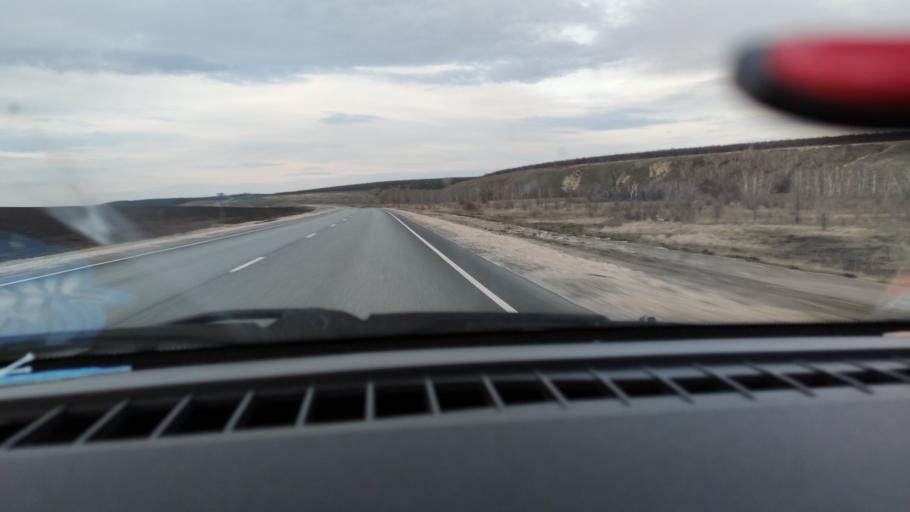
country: RU
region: Saratov
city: Yelshanka
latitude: 51.8600
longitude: 46.4978
